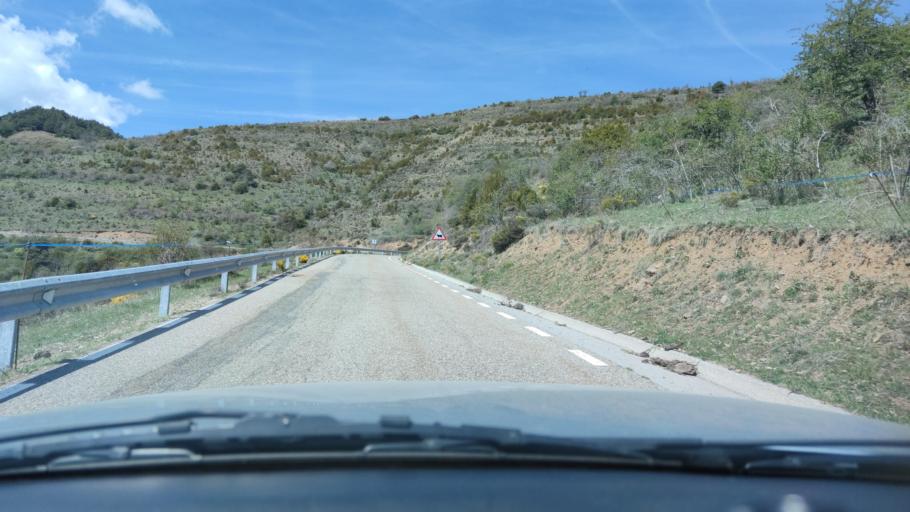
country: ES
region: Catalonia
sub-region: Provincia de Lleida
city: Coll de Nargo
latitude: 42.2956
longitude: 1.2340
